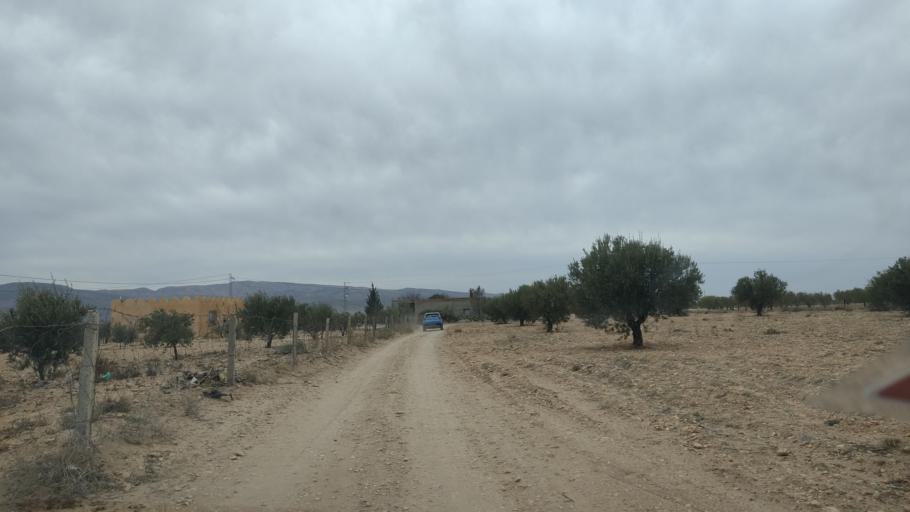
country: TN
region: Al Qasrayn
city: Kasserine
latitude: 35.2290
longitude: 8.9263
